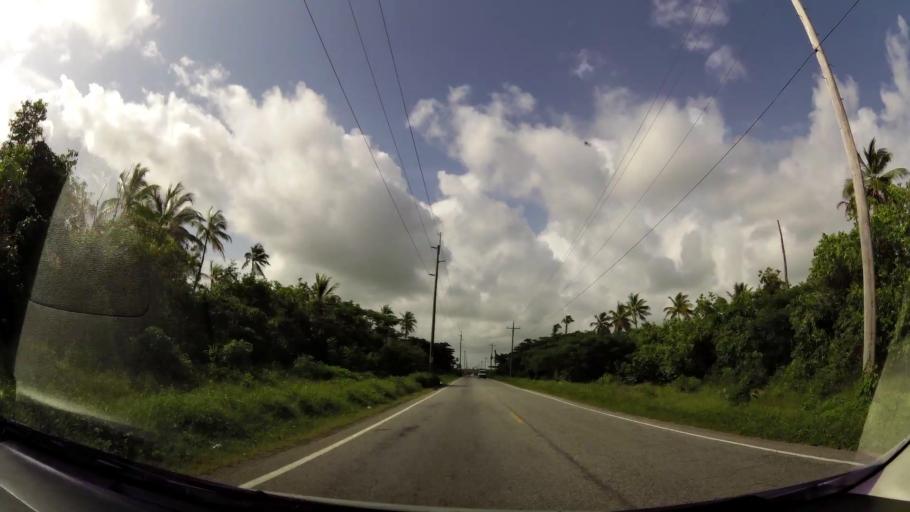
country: GY
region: Demerara-Mahaica
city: Mahaica Village
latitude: 6.6912
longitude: -57.9294
